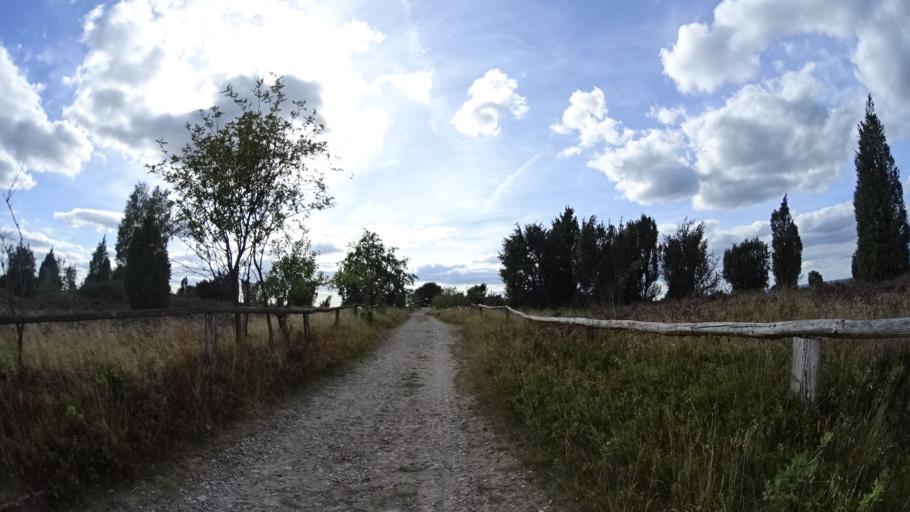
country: DE
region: Lower Saxony
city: Undeloh
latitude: 53.1675
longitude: 9.9422
